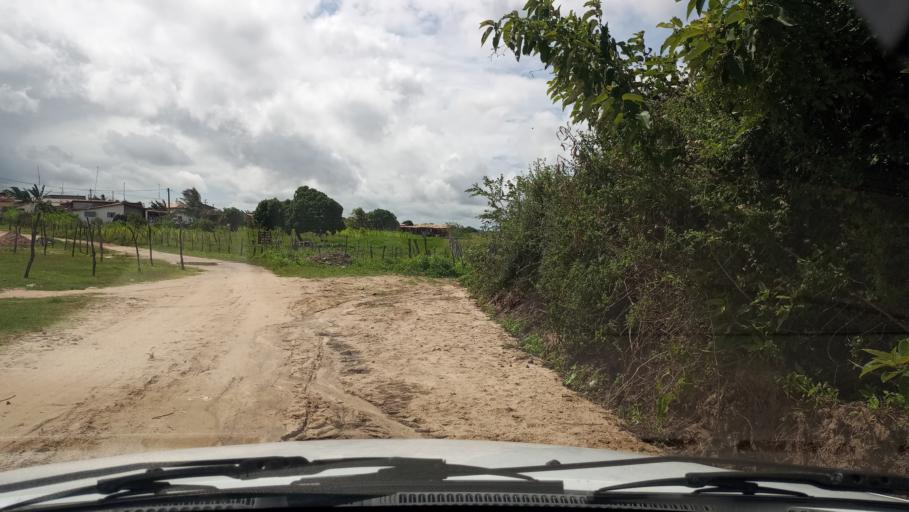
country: BR
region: Rio Grande do Norte
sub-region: Brejinho
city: Brejinho
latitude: -6.1587
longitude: -35.4401
